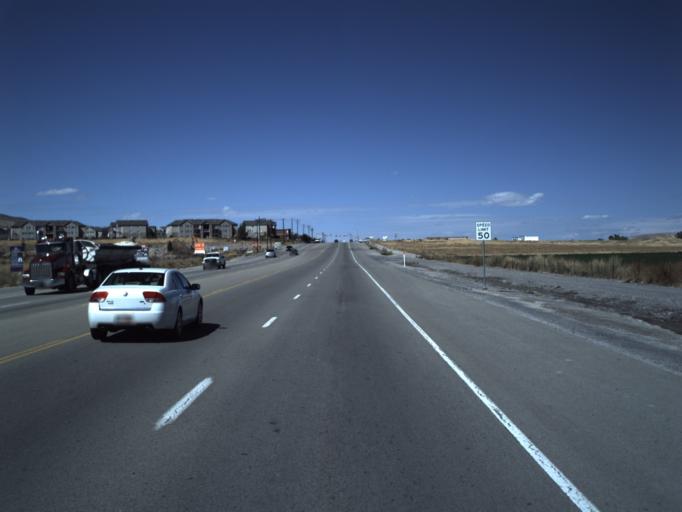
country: US
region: Utah
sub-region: Utah County
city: Saratoga Springs
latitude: 40.3929
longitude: -111.9173
